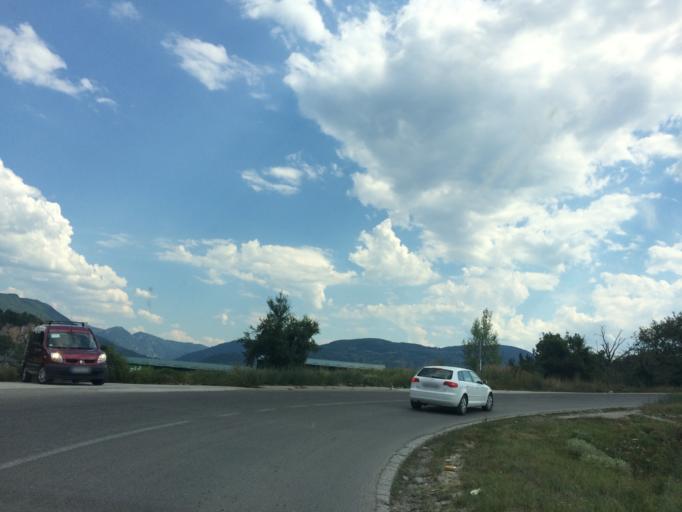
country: RS
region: Central Serbia
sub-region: Zlatiborski Okrug
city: Prijepolje
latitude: 43.3611
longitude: 19.6350
